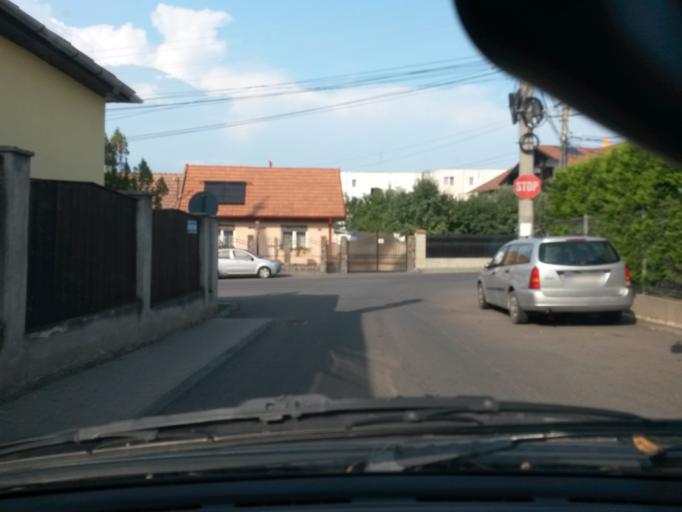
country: RO
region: Mures
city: Targu-Mures
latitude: 46.5322
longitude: 24.5833
